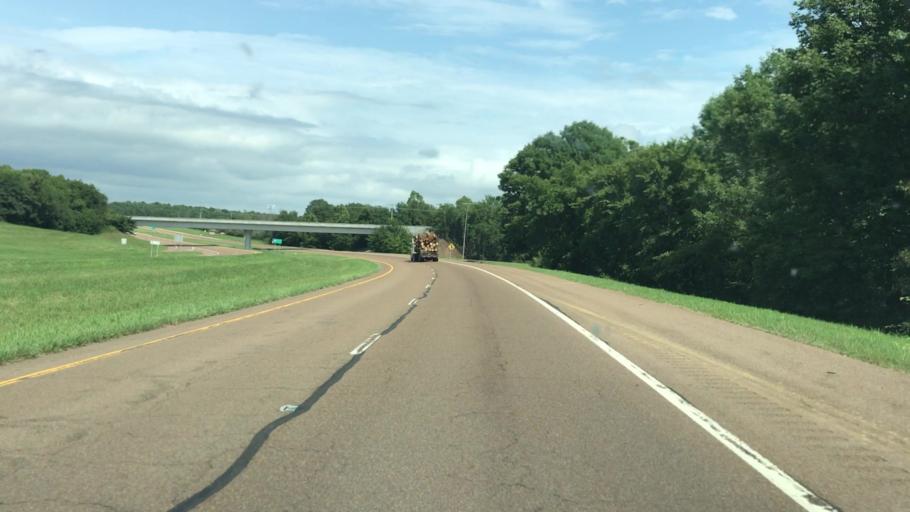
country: US
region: Tennessee
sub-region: Obion County
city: South Fulton
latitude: 36.4949
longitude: -88.9080
